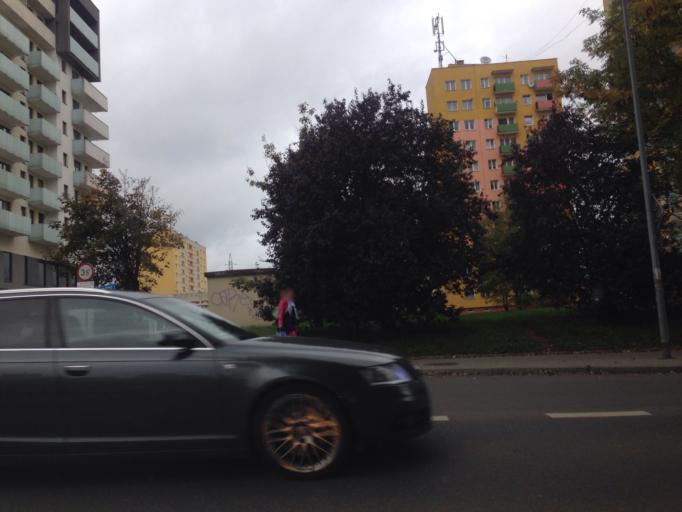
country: PL
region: Pomeranian Voivodeship
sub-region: Gdansk
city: Gdansk
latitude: 54.3877
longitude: 18.6239
